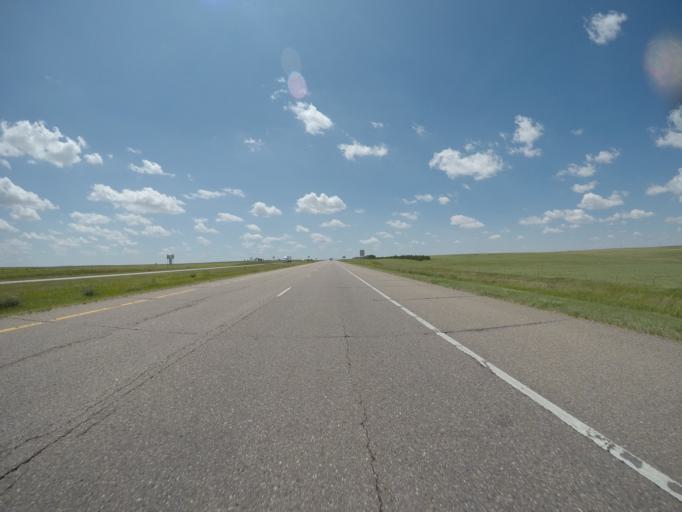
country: US
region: Colorado
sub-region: Lincoln County
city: Hugo
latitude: 39.2924
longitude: -102.8871
